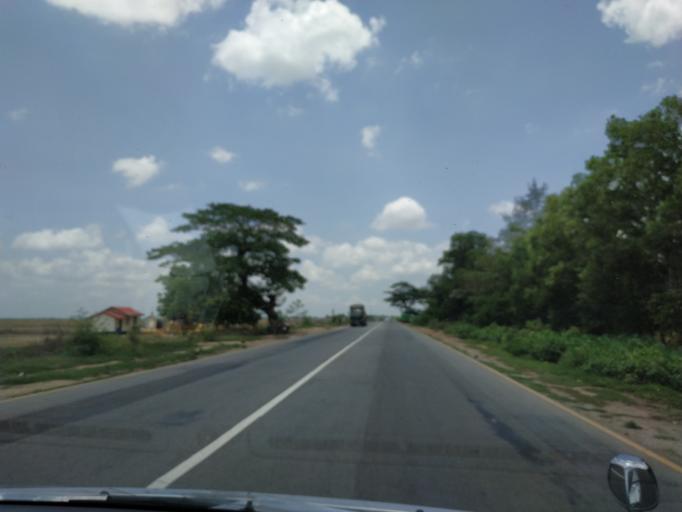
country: MM
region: Bago
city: Thanatpin
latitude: 17.4606
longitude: 96.5975
